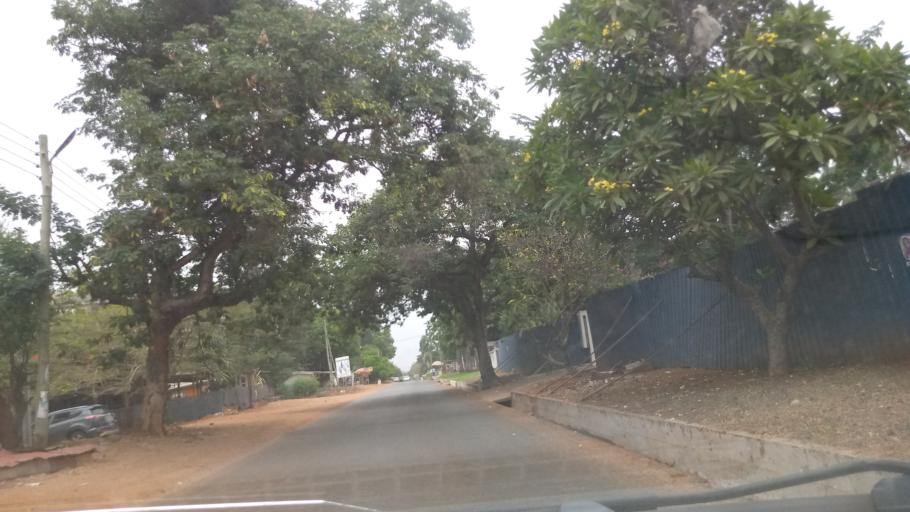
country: GH
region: Greater Accra
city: Accra
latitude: 5.6060
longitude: -0.1876
